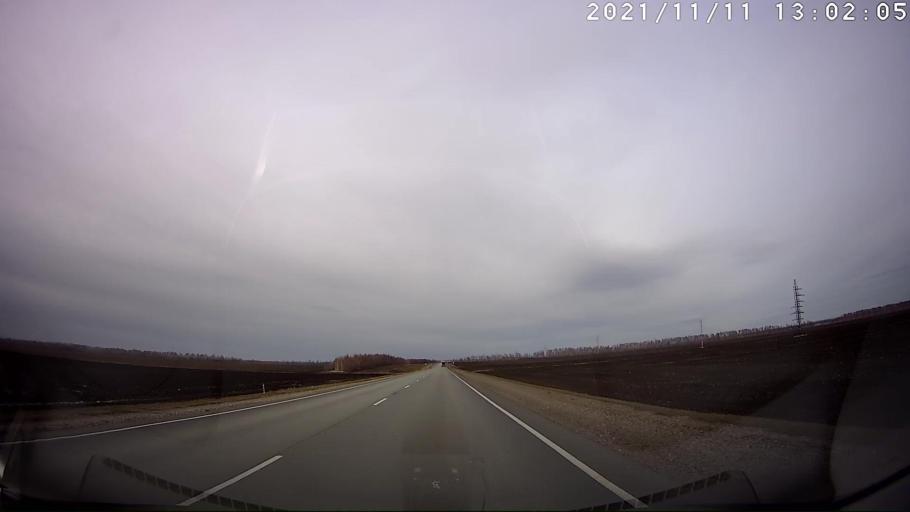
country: RU
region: Ulyanovsk
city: Isheyevka
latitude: 54.3908
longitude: 48.1901
